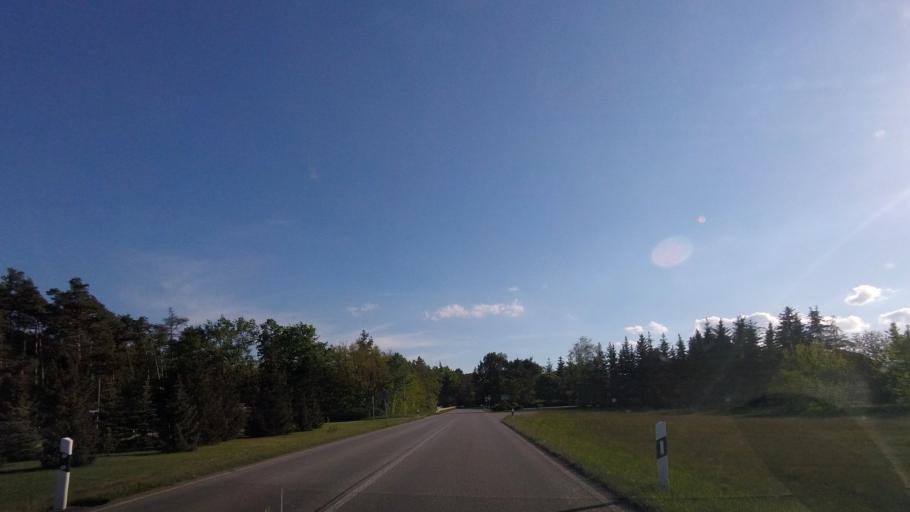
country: DE
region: Brandenburg
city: Luebben
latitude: 51.9102
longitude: 13.8634
